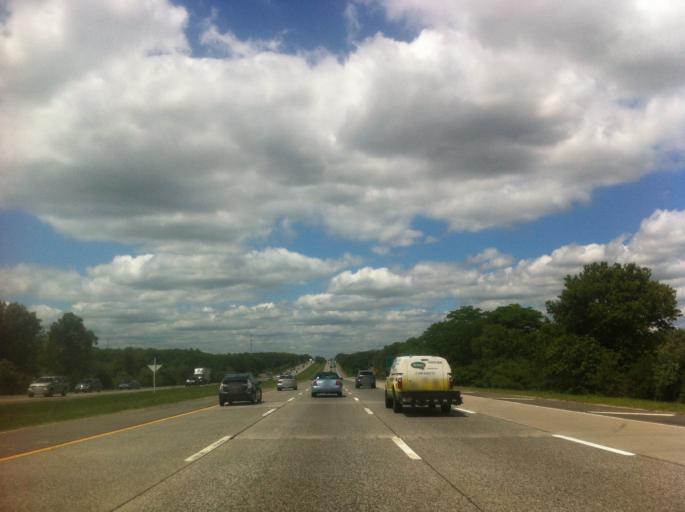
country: US
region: New York
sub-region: Suffolk County
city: Yaphank
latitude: 40.8311
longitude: -72.9254
